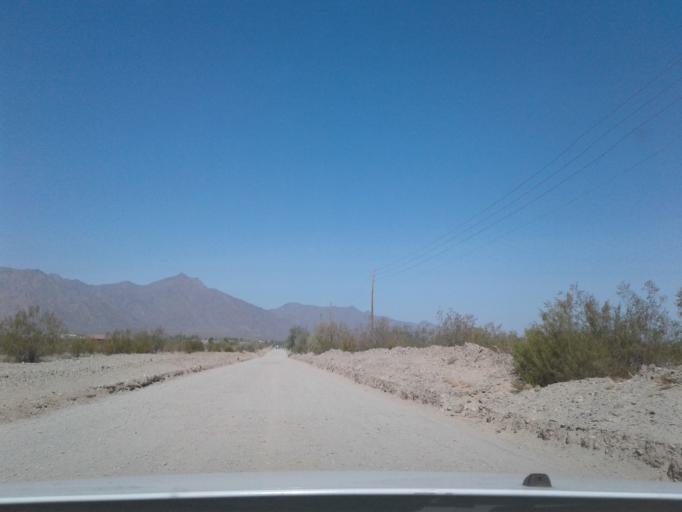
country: US
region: Arizona
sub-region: Maricopa County
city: Laveen
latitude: 33.2905
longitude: -112.1467
